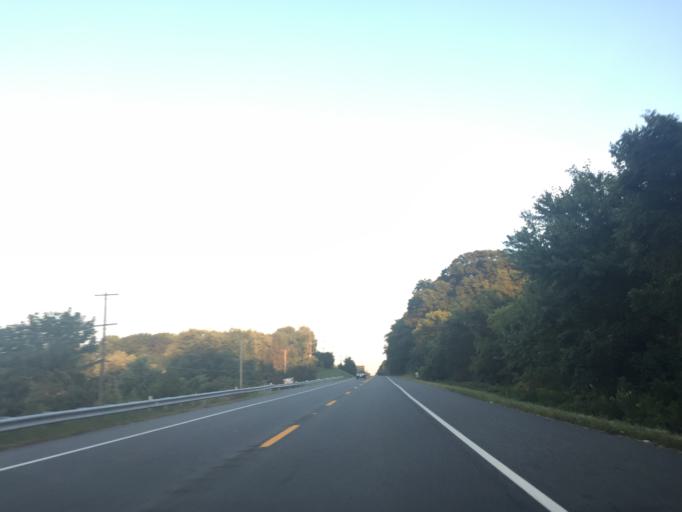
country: US
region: Pennsylvania
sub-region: York County
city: Susquehanna Trails
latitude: 39.7002
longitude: -76.3295
